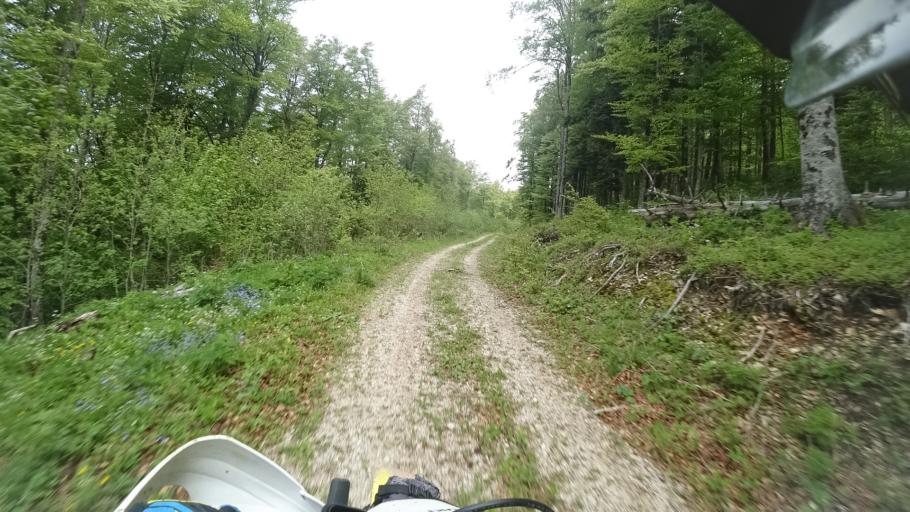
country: BA
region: Federation of Bosnia and Herzegovina
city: Orasac
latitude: 44.5721
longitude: 15.8694
